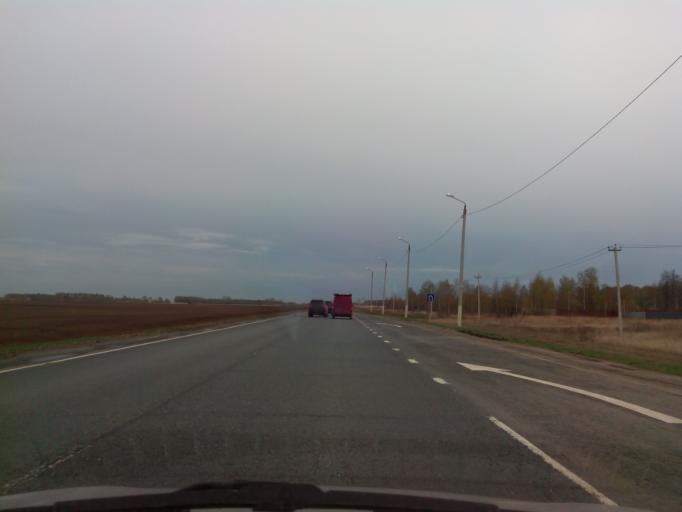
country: RU
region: Moskovskaya
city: Ozherel'ye
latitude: 54.6473
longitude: 38.3624
